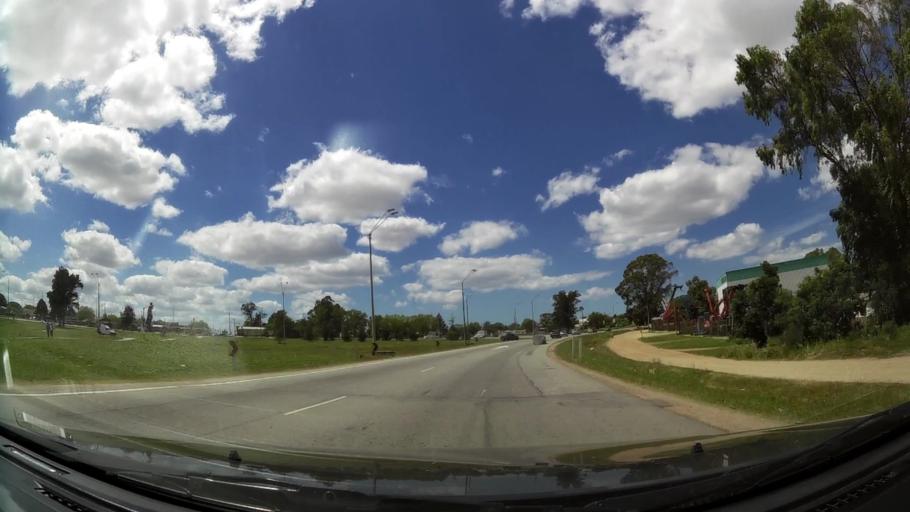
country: UY
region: Canelones
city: Colonia Nicolich
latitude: -34.8195
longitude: -56.0102
